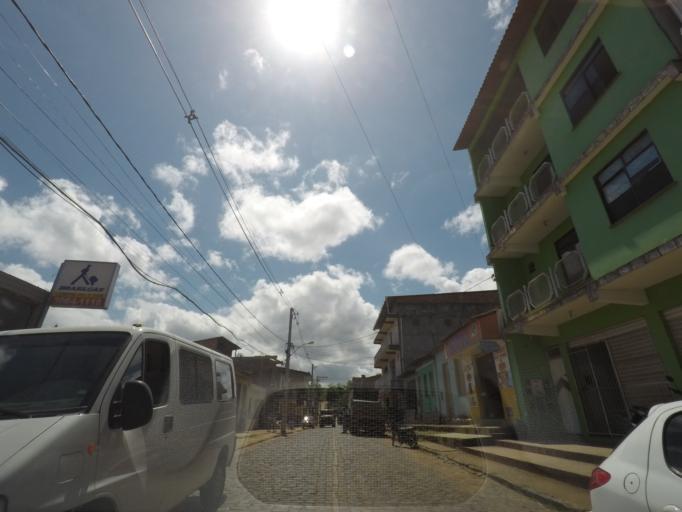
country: BR
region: Bahia
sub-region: Taperoa
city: Taperoa
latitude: -13.5379
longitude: -39.1003
